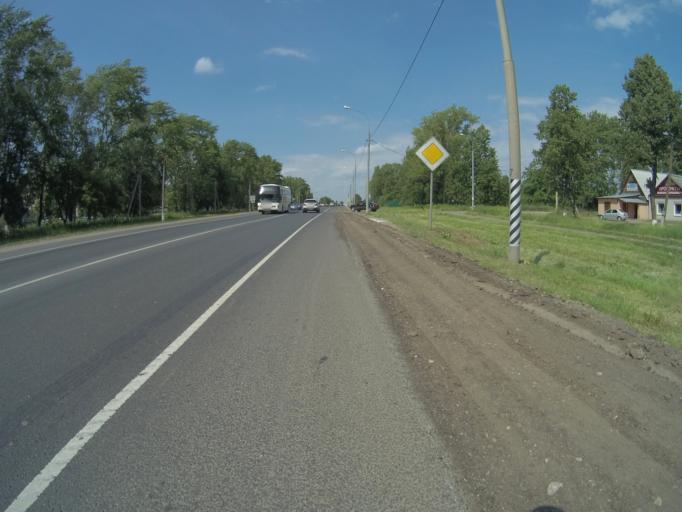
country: RU
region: Vladimir
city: Suzdal'
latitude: 56.3237
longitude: 40.4724
